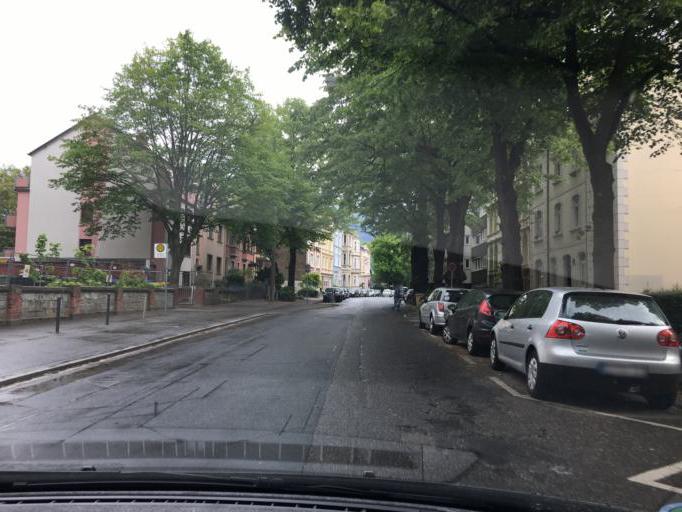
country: DE
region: North Rhine-Westphalia
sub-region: Regierungsbezirk Koln
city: Bonn
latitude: 50.7459
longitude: 7.0952
